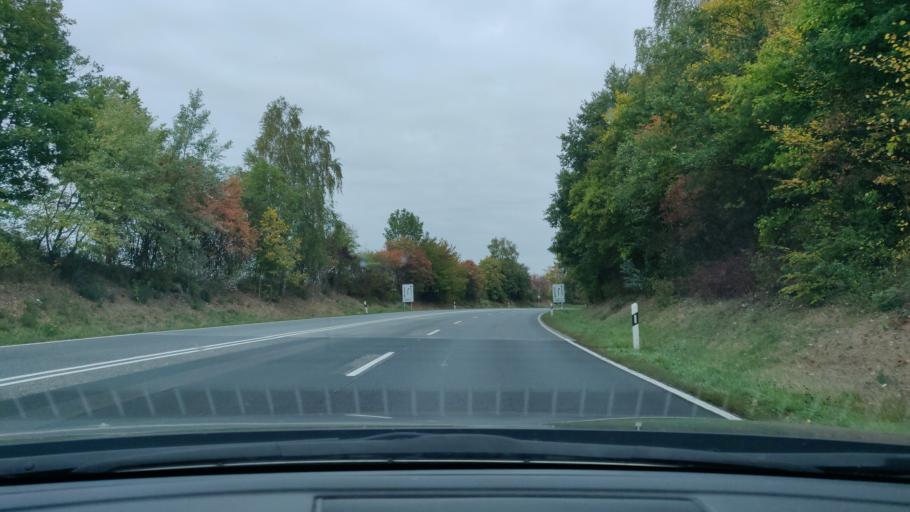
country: DE
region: Hesse
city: Schwalmstadt
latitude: 50.9279
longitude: 9.2559
